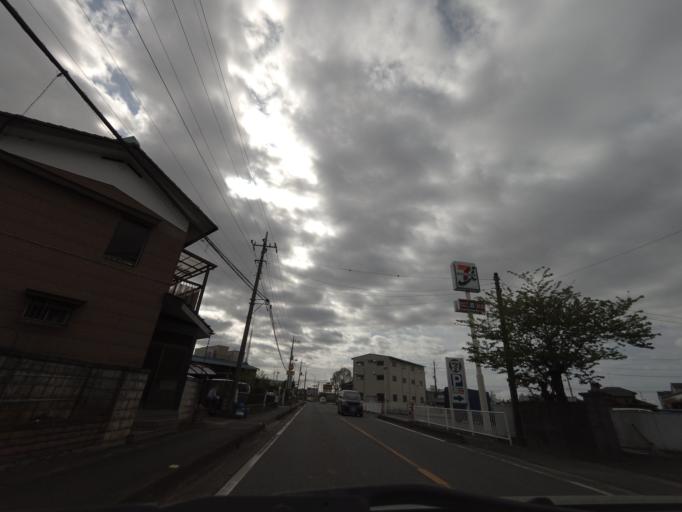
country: JP
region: Saitama
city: Kamifukuoka
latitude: 35.8835
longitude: 139.5453
